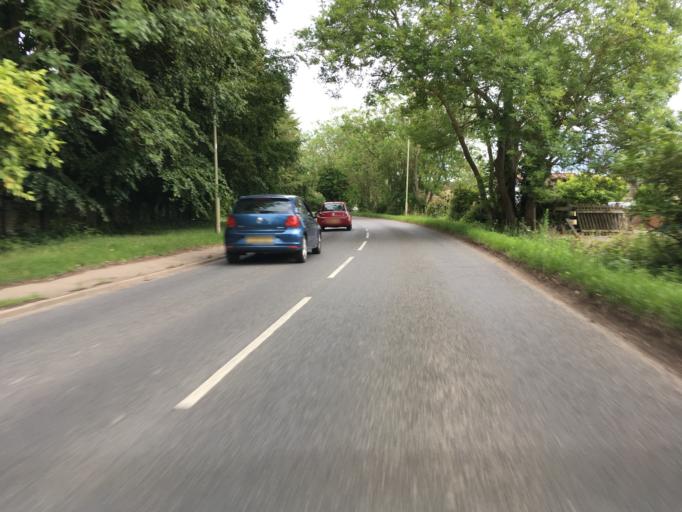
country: GB
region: England
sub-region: Oxfordshire
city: Boars Hill
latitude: 51.6992
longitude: -1.3029
